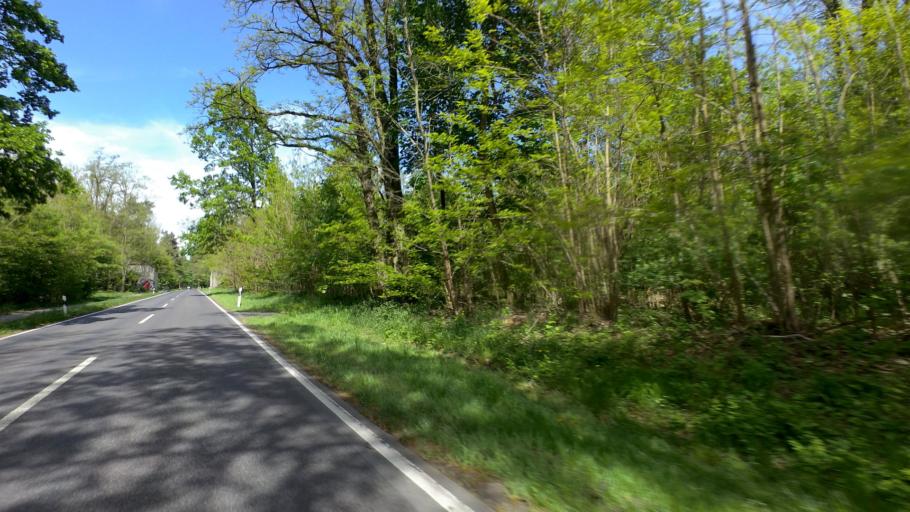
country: DE
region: Brandenburg
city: Sperenberg
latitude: 52.1593
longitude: 13.3659
